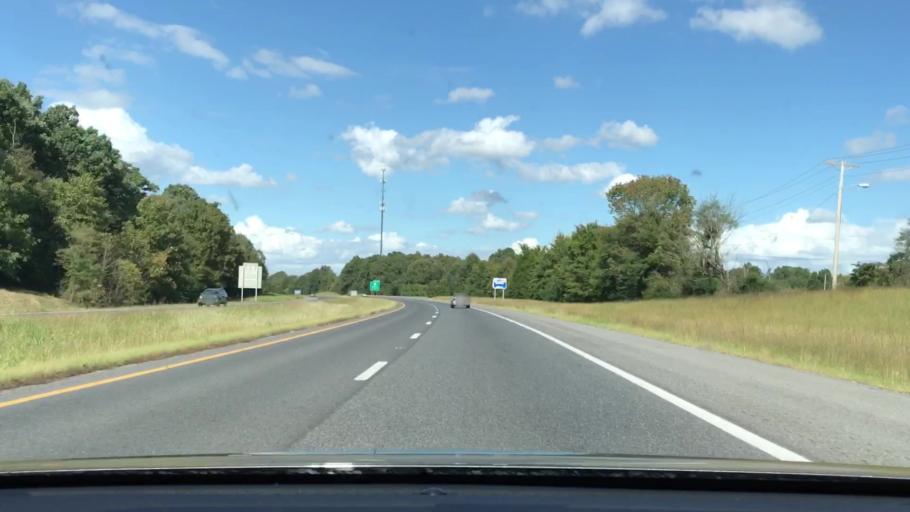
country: US
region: Kentucky
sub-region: Marshall County
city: Benton
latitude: 36.8540
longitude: -88.3695
